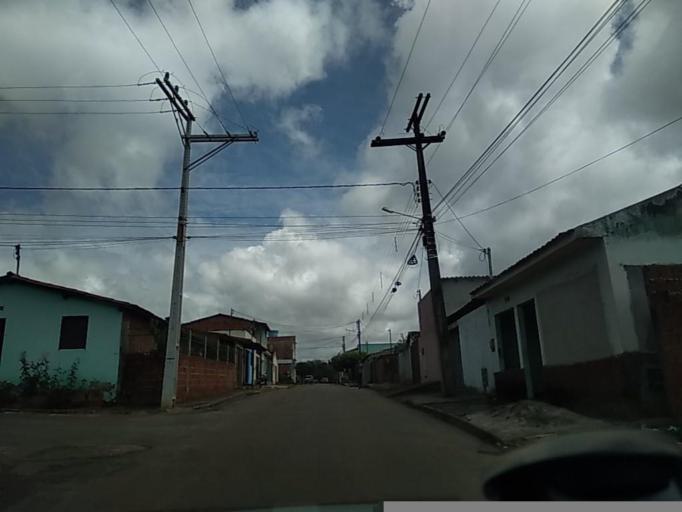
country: BR
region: Bahia
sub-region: Caetite
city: Caetite
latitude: -14.0565
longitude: -42.4829
